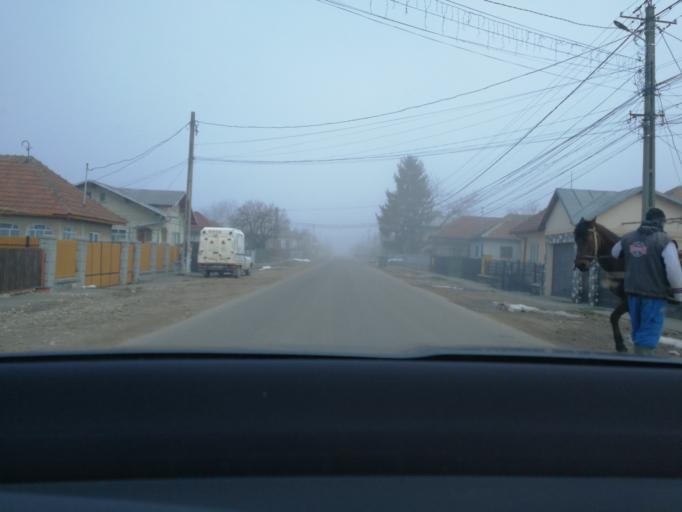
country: RO
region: Prahova
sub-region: Comuna Magureni
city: Lunca Prahovei
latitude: 45.0456
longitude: 25.7506
